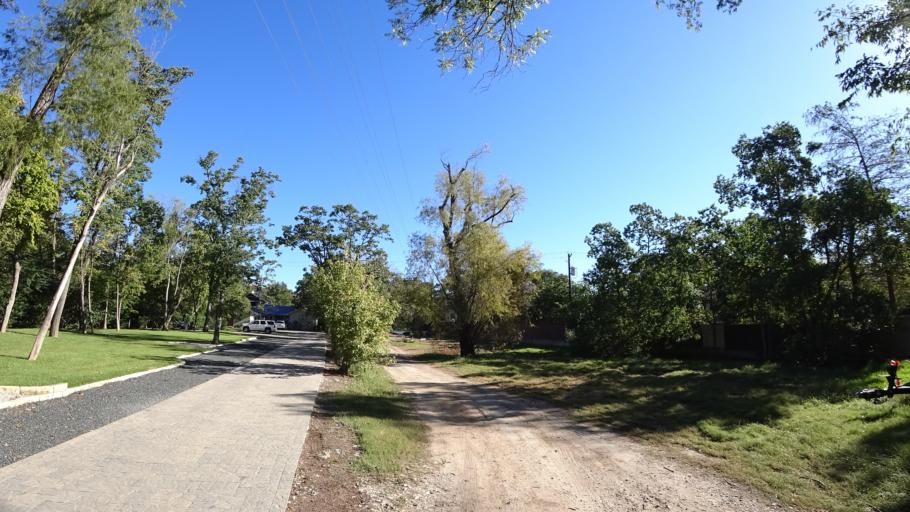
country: US
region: Texas
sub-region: Travis County
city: West Lake Hills
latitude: 30.3355
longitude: -97.7856
